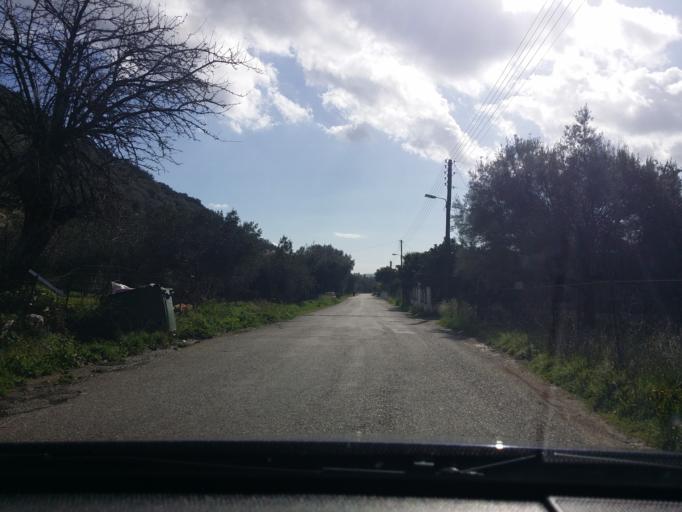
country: GR
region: West Greece
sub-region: Nomos Aitolias kai Akarnanias
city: Astakos
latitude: 38.5903
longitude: 21.0891
